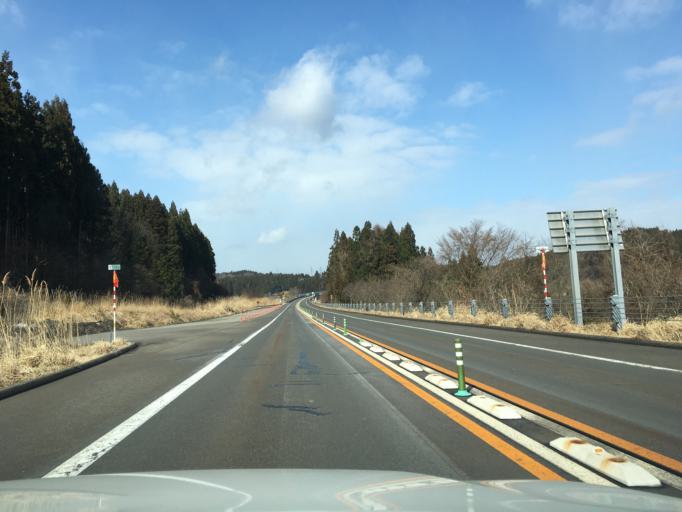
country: JP
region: Akita
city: Akita
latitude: 39.7526
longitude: 140.1445
